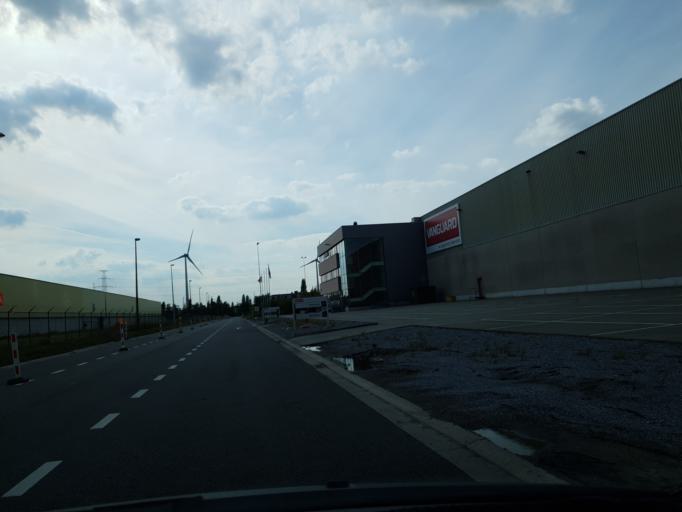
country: BE
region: Flanders
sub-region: Provincie Antwerpen
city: Antwerpen
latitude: 51.2674
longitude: 4.3900
